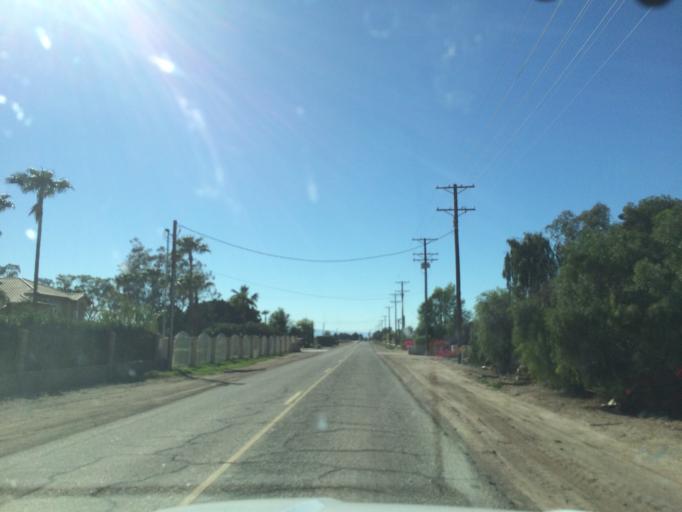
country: US
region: California
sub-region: Imperial County
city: Heber
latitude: 32.7524
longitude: -115.5376
